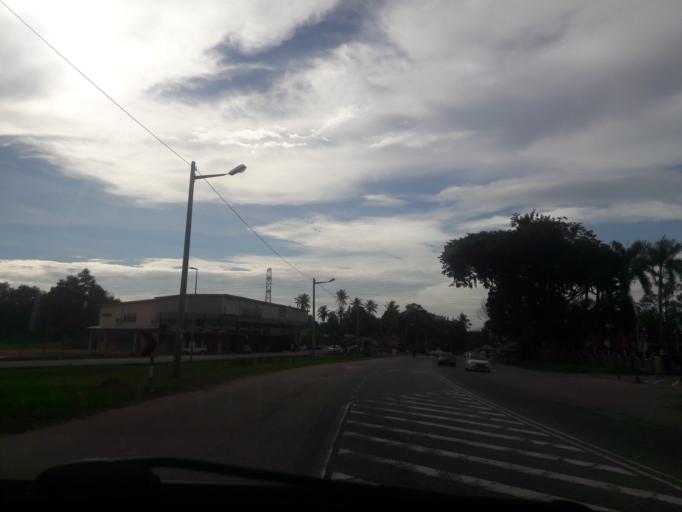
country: MY
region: Kedah
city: Sungai Petani
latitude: 5.6258
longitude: 100.5290
